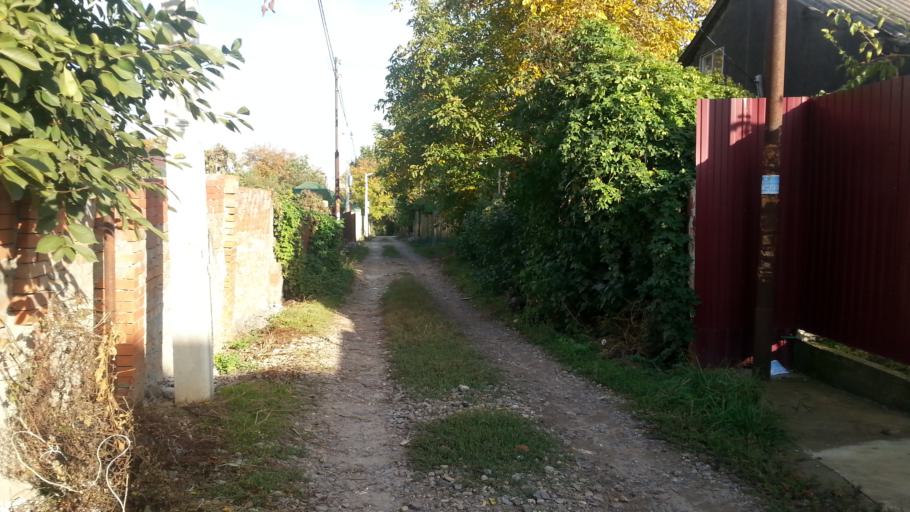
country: RU
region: Rostov
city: Severnyy
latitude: 47.2895
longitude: 39.6687
